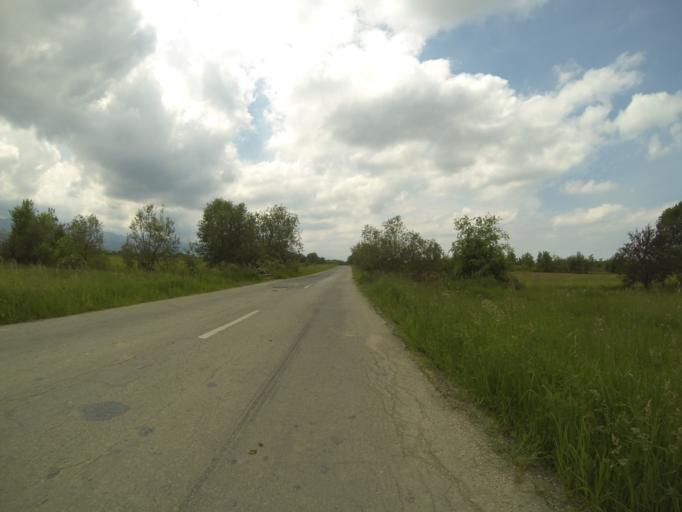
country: RO
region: Brasov
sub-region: Comuna Harseni
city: Harseni
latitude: 45.7357
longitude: 25.0545
